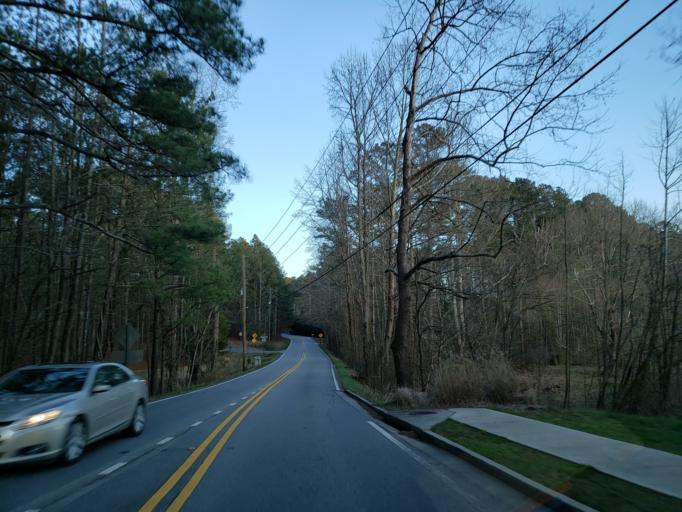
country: US
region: Georgia
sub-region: Cobb County
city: Acworth
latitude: 33.9999
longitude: -84.7353
